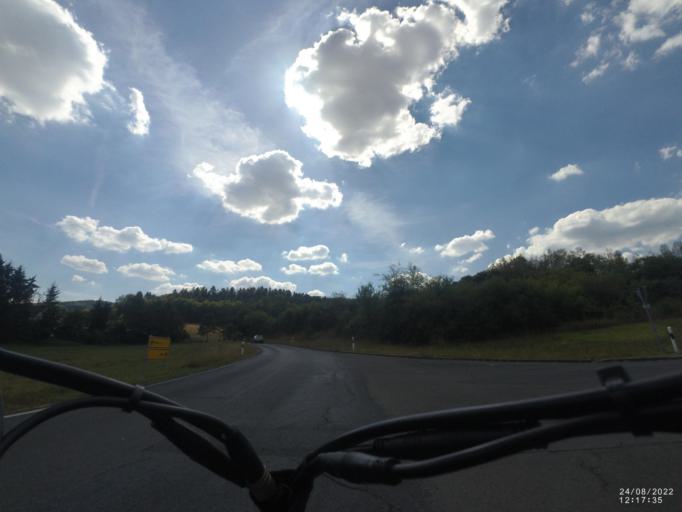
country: DE
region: Rheinland-Pfalz
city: Pelm
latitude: 50.2221
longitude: 6.6906
